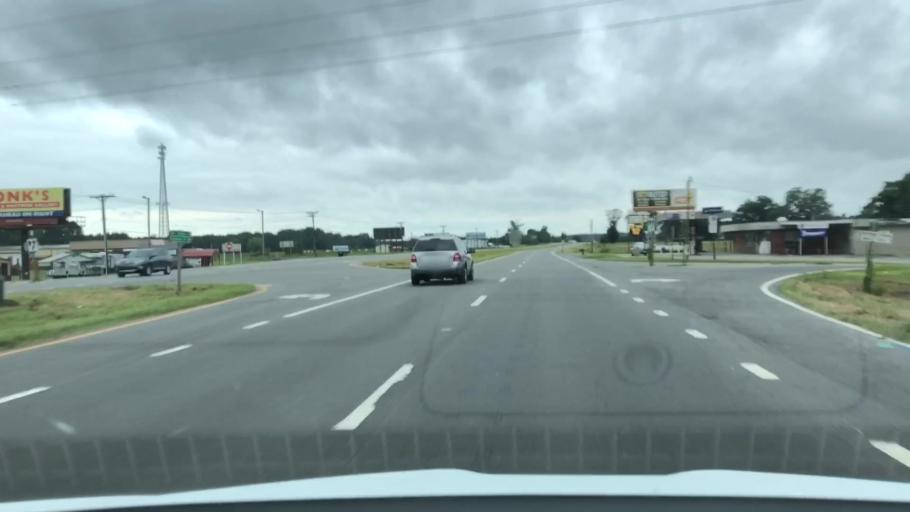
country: US
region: North Carolina
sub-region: Lenoir County
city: La Grange
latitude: 35.2610
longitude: -77.6934
